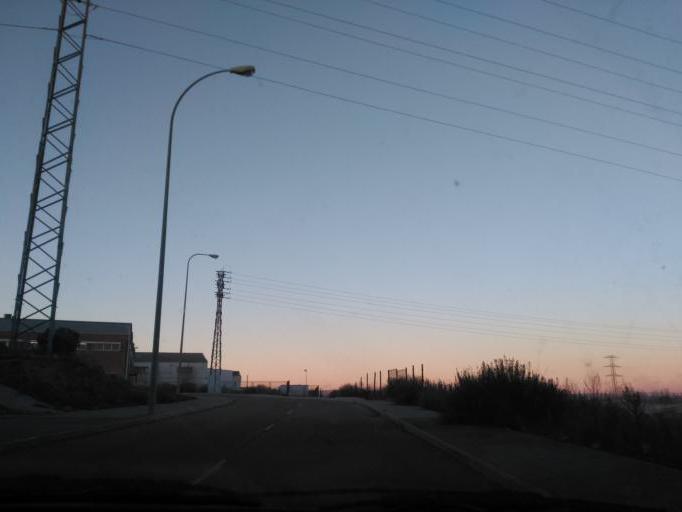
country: ES
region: Castille and Leon
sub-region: Provincia de Salamanca
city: Carbajosa de la Sagrada
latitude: 40.9428
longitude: -5.6512
